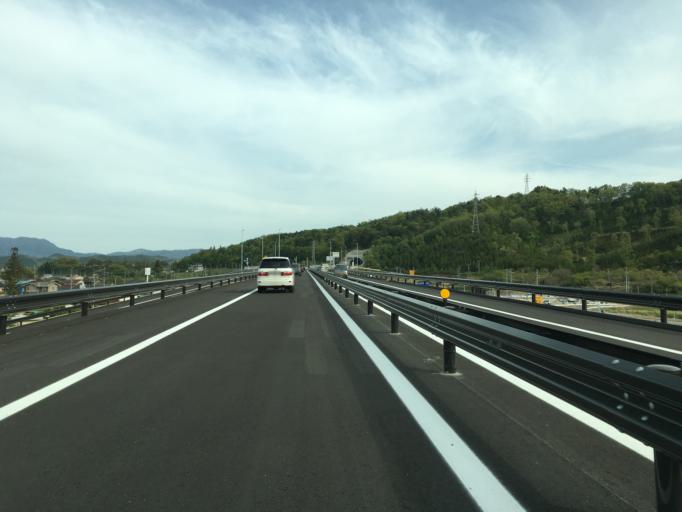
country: JP
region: Fukushima
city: Hobaramachi
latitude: 37.8124
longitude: 140.5356
